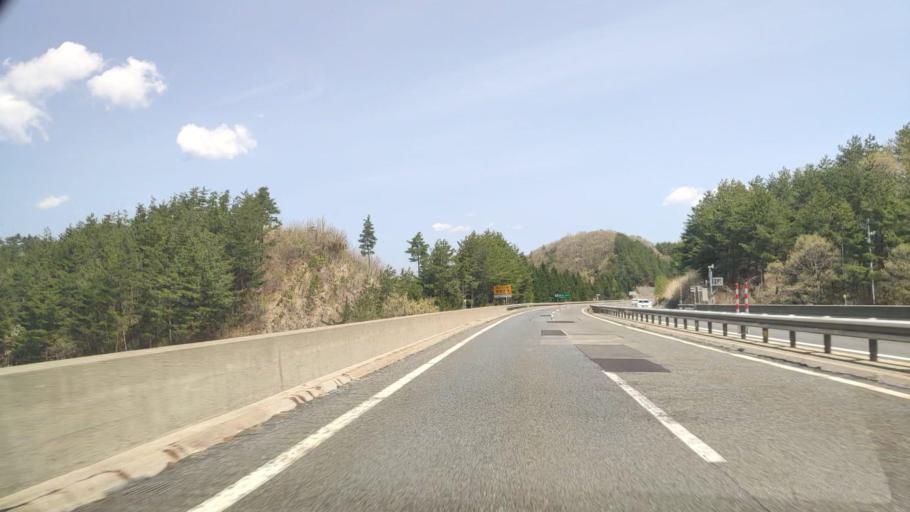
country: JP
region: Iwate
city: Ichinohe
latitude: 40.3111
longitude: 141.4315
